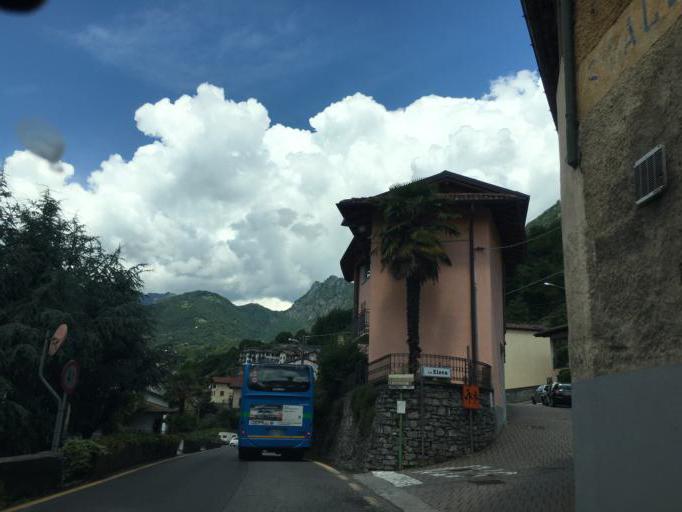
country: IT
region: Lombardy
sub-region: Provincia di Como
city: Carlazzo
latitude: 46.0411
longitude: 9.1734
